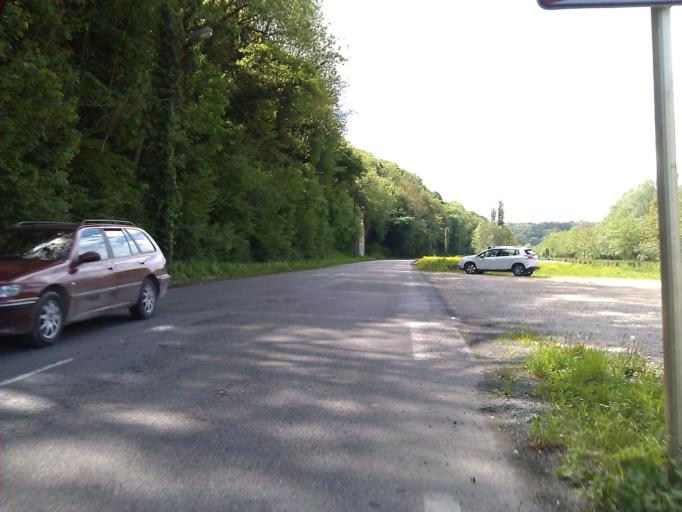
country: FR
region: Franche-Comte
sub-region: Departement du Doubs
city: Courcelles-les-Montbeliard
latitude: 47.5036
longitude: 6.7889
